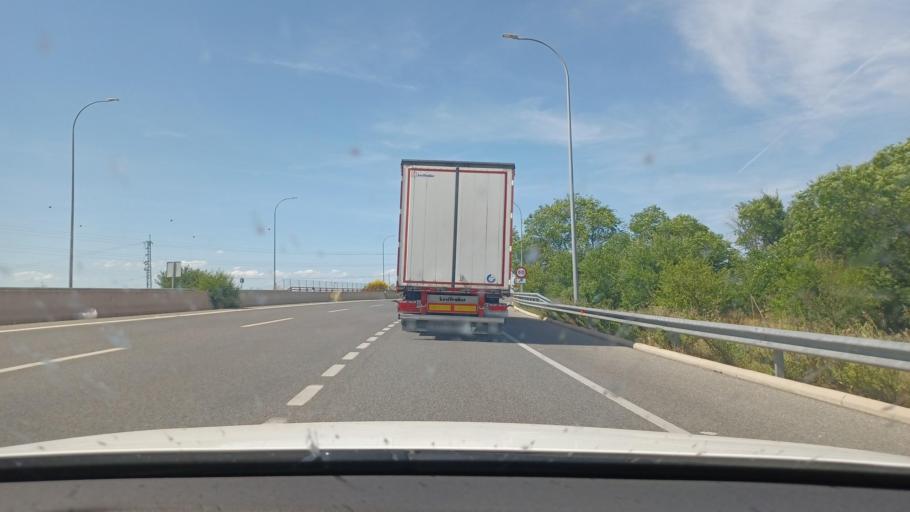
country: ES
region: Madrid
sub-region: Provincia de Madrid
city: Torrejon de Ardoz
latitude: 40.4709
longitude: -3.4178
